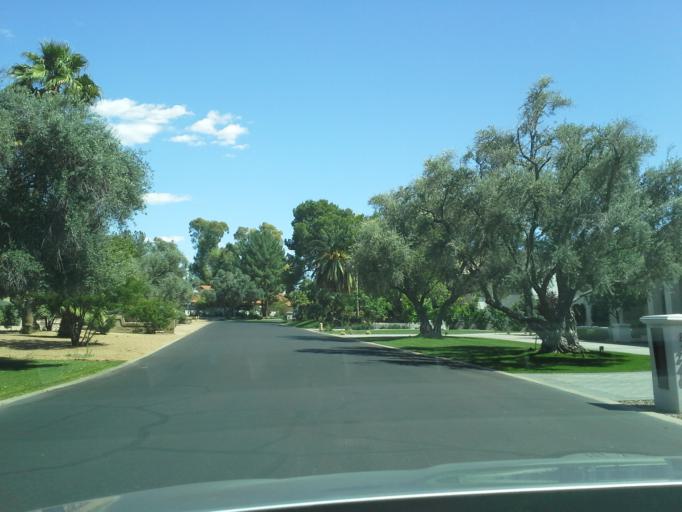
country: US
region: Arizona
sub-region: Maricopa County
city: Paradise Valley
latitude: 33.5576
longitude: -111.9288
